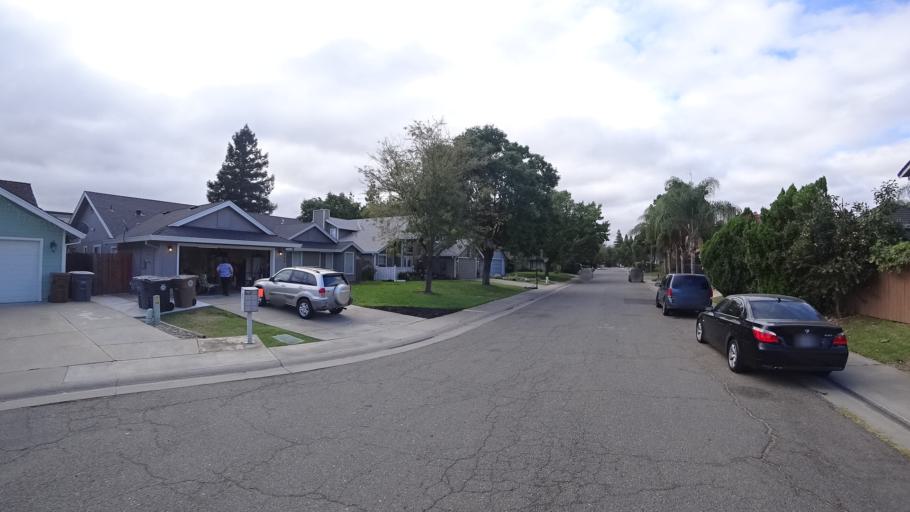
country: US
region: California
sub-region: Sacramento County
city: Laguna
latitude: 38.4227
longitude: -121.4198
